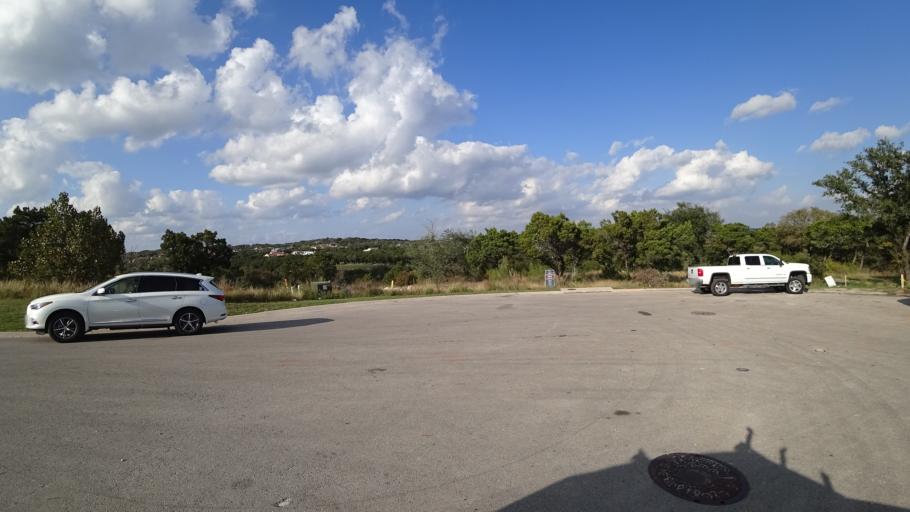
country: US
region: Texas
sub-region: Travis County
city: Barton Creek
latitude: 30.2738
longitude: -97.8738
